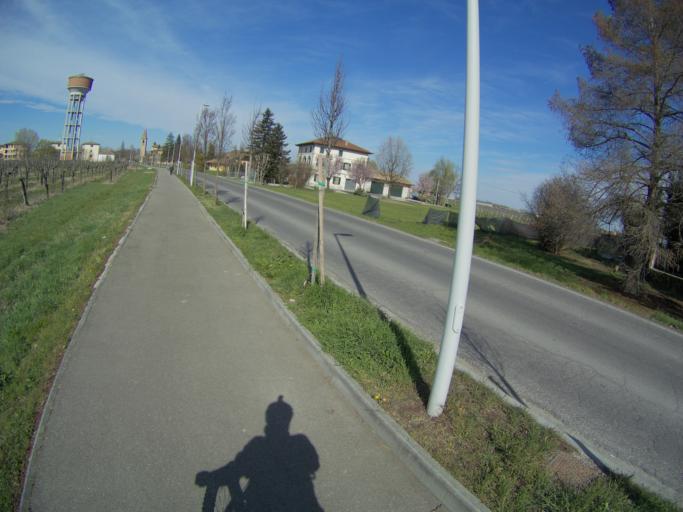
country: IT
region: Emilia-Romagna
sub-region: Provincia di Reggio Emilia
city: Massenzatico
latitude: 44.7235
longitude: 10.6958
